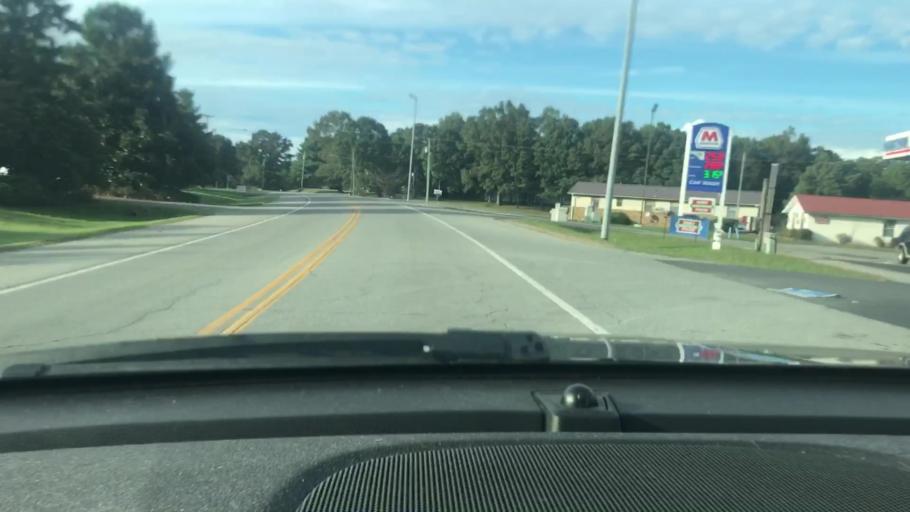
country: US
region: Tennessee
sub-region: Dickson County
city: White Bluff
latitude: 36.1261
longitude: -87.2275
